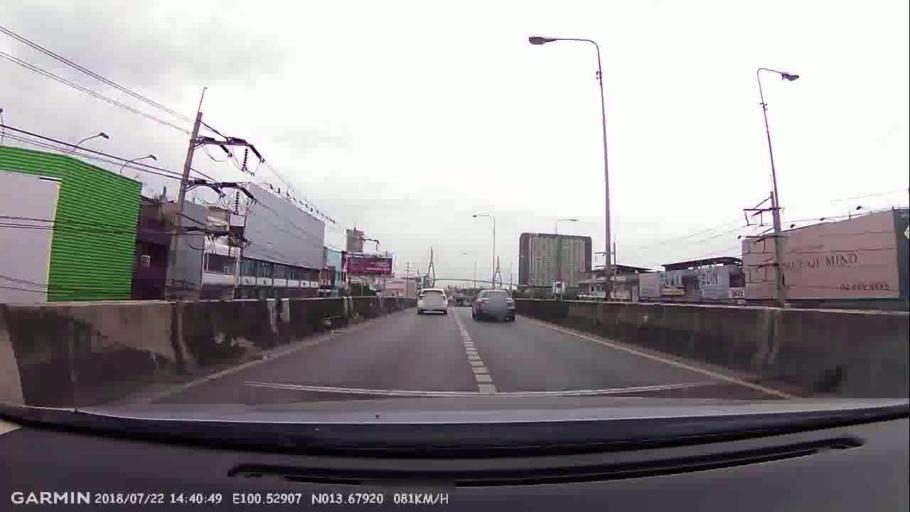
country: TH
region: Samut Prakan
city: Phra Pradaeng
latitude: 13.6791
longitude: 100.5292
